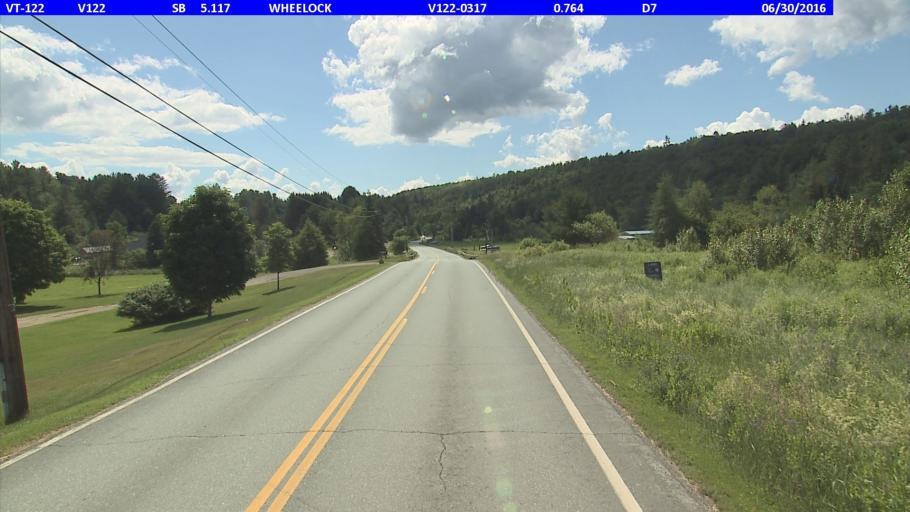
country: US
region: Vermont
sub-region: Caledonia County
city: Lyndonville
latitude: 44.5842
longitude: -72.0776
